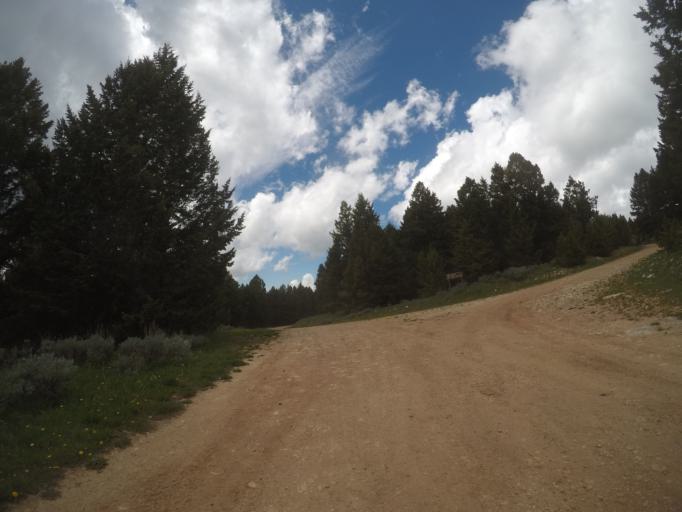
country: US
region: Wyoming
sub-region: Big Horn County
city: Lovell
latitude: 45.1622
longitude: -108.4022
